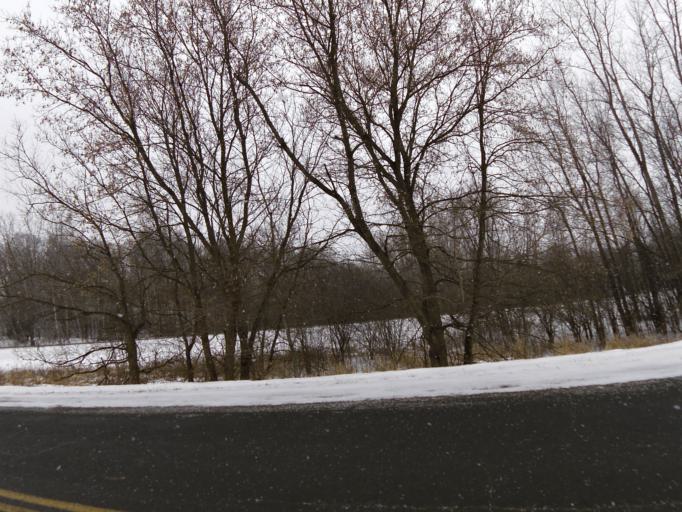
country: US
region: Minnesota
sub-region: Washington County
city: Lake Elmo
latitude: 44.9649
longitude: -92.8452
